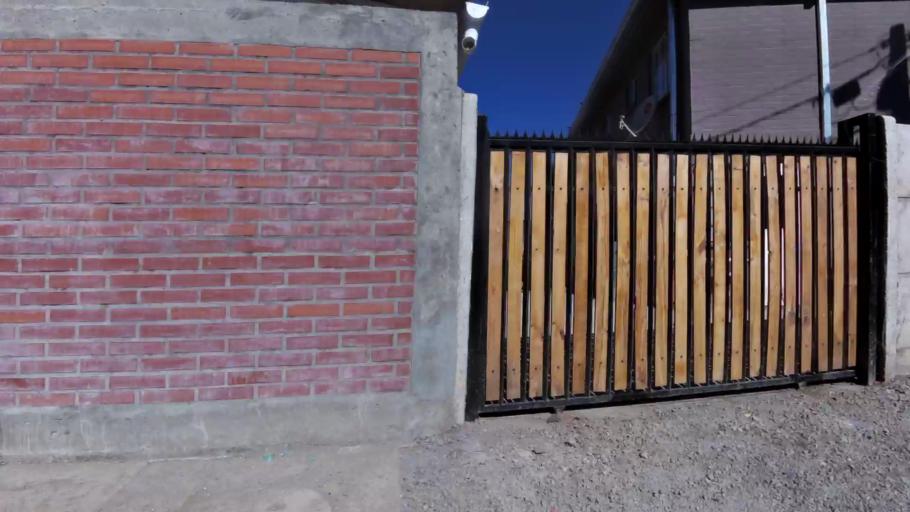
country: CL
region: O'Higgins
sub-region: Provincia de Cachapoal
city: Rancagua
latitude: -34.1770
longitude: -70.7713
